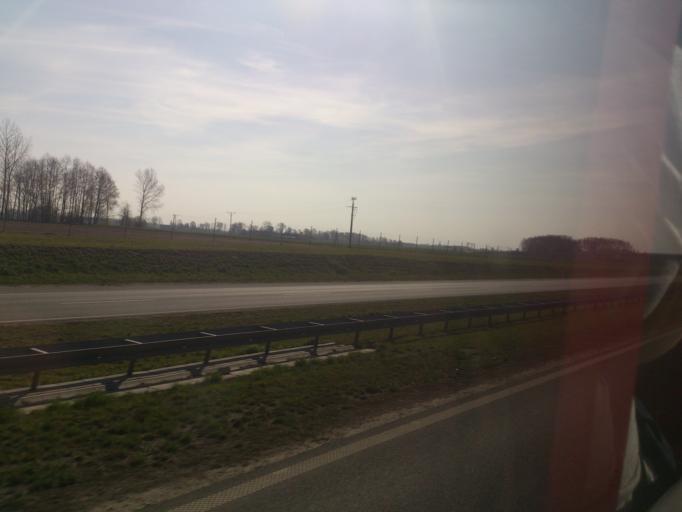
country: PL
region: Lodz Voivodeship
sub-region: Powiat kutnowski
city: Lanieta
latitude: 52.4164
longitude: 19.2633
